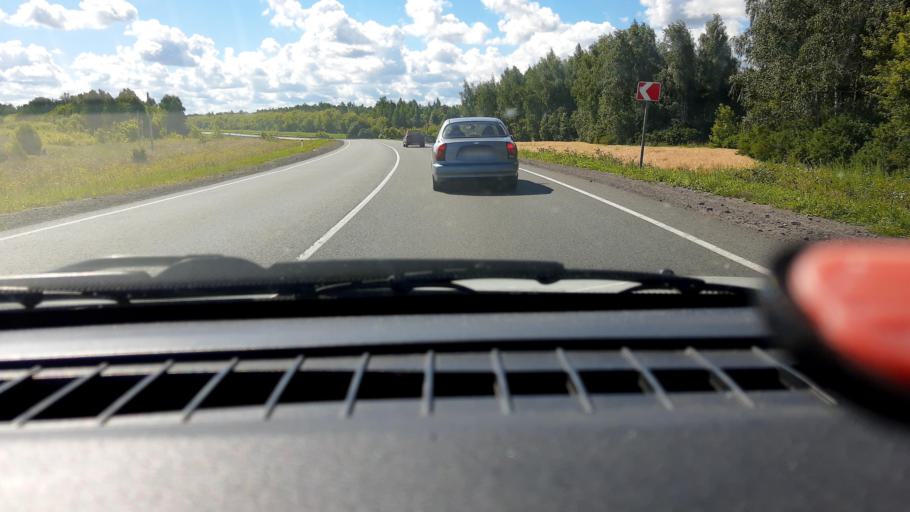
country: RU
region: Nizjnij Novgorod
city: Arzamas
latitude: 55.3192
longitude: 43.8891
